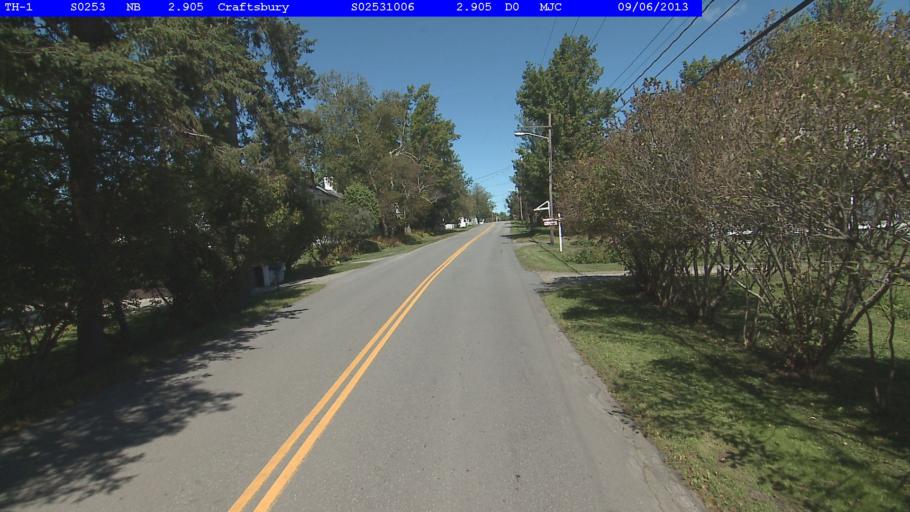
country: US
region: Vermont
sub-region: Caledonia County
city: Hardwick
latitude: 44.6500
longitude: -72.3814
